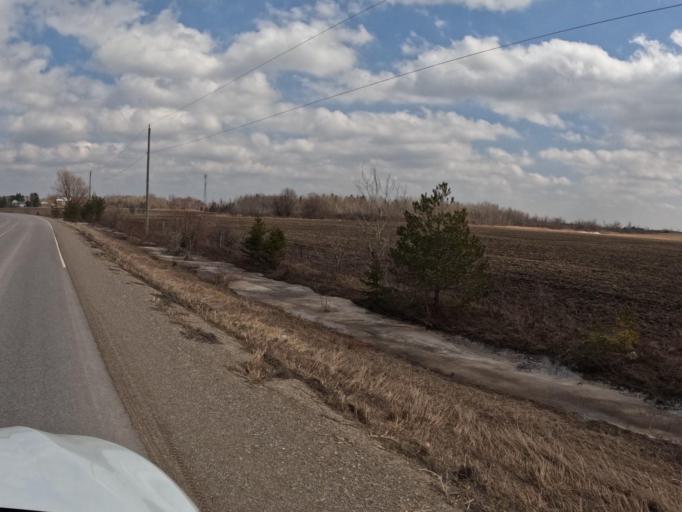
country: CA
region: Ontario
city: Shelburne
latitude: 44.0038
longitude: -80.2316
